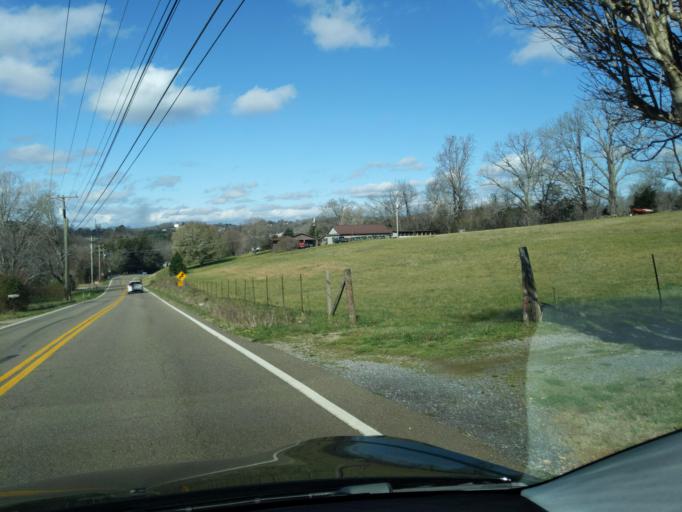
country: US
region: Tennessee
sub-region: Sevier County
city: Sevierville
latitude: 35.9718
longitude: -83.5332
